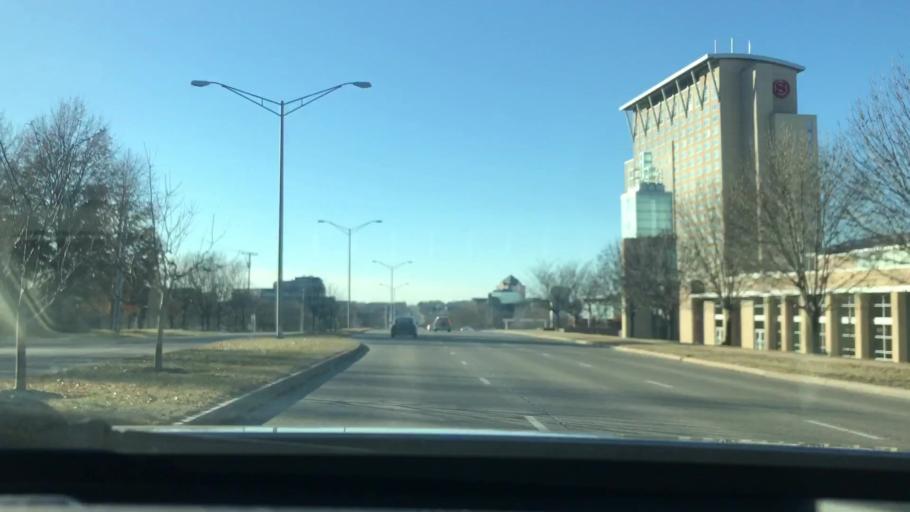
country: US
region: Kansas
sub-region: Johnson County
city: Leawood
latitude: 38.9277
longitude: -94.6544
